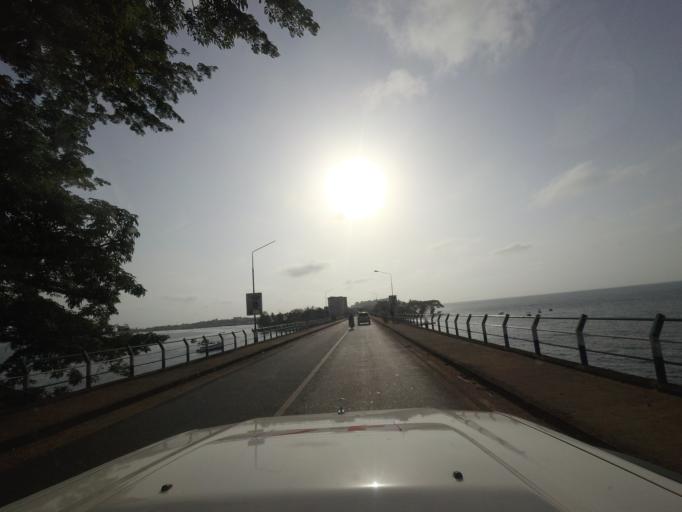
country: SL
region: Western Area
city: Freetown
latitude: 8.4924
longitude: -13.2723
